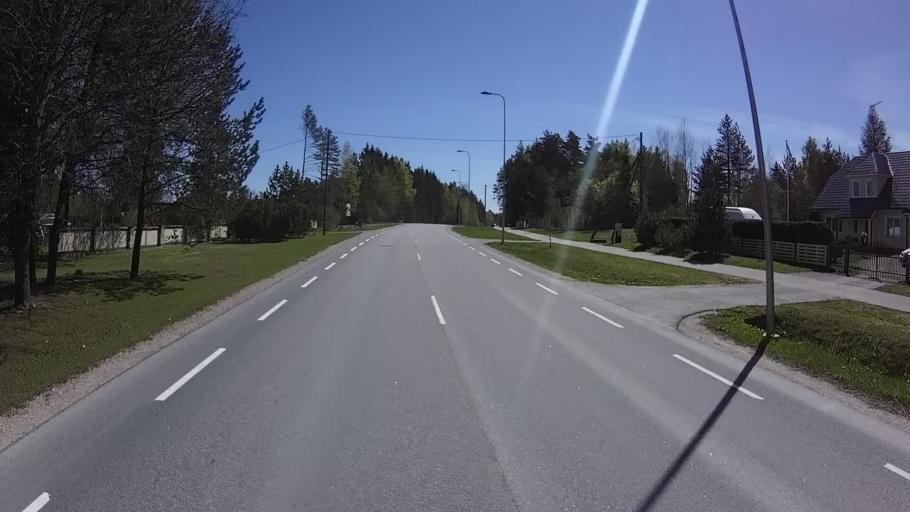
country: EE
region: Harju
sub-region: Raasiku vald
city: Raasiku
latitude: 59.1719
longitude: 25.1728
